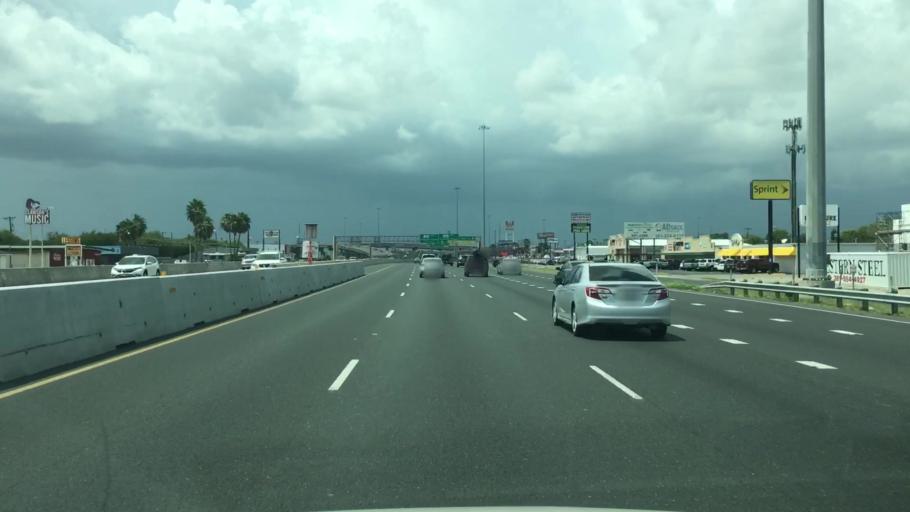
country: US
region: Texas
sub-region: Nueces County
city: Corpus Christi
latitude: 27.7326
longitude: -97.4207
